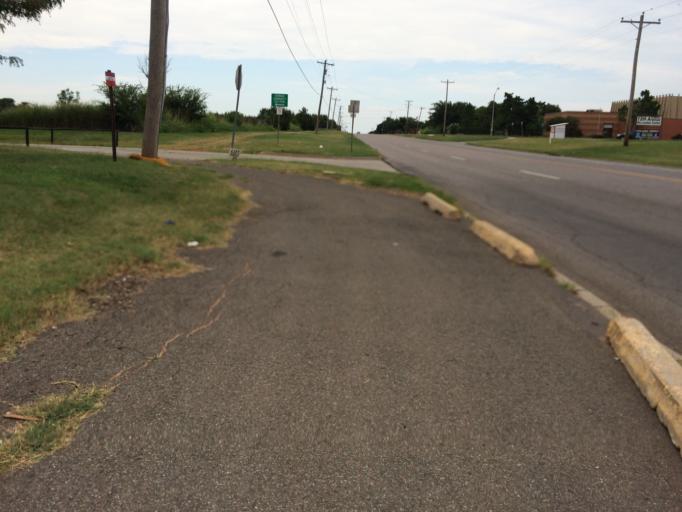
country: US
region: Oklahoma
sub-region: Cleveland County
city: Hall Park
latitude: 35.2381
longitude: -97.4237
